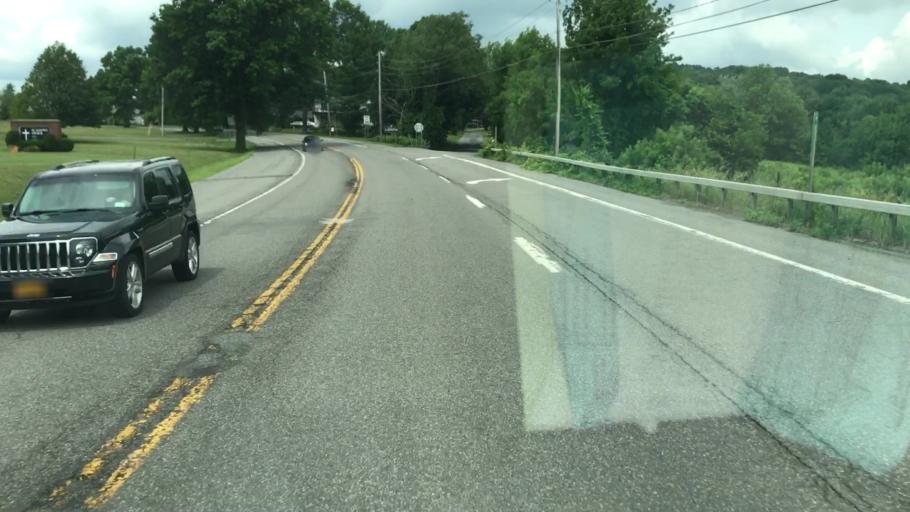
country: US
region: New York
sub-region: Onondaga County
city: Nedrow
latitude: 42.8895
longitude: -76.0958
